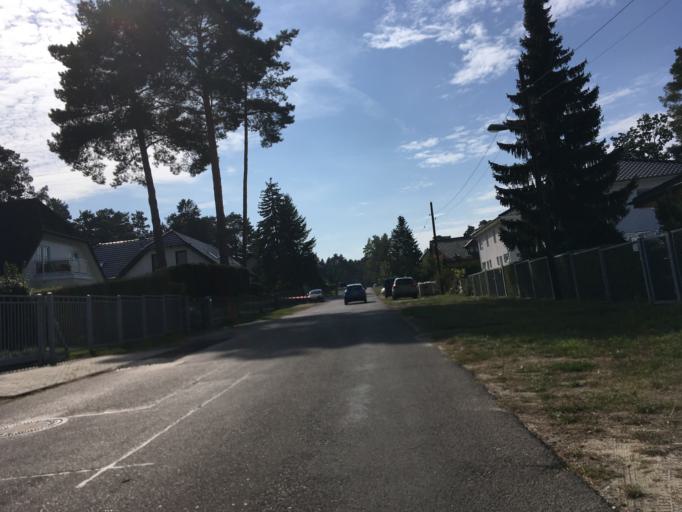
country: DE
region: Berlin
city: Muggelheim
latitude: 52.4123
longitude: 13.6509
